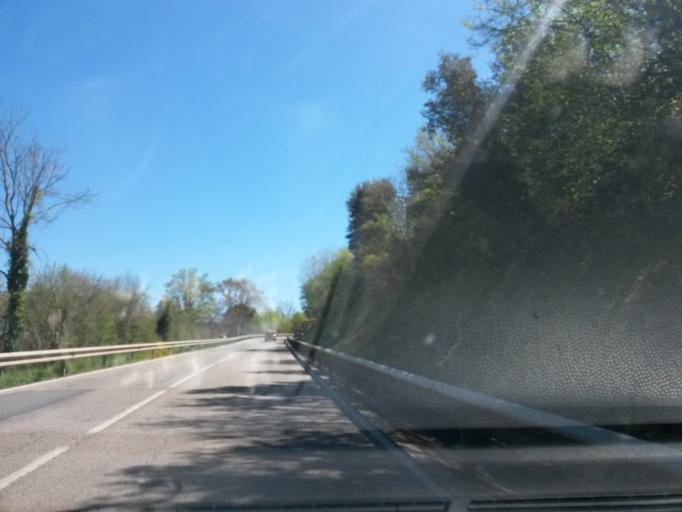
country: ES
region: Catalonia
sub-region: Provincia de Girona
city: Santa Pau
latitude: 42.1495
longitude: 2.5405
